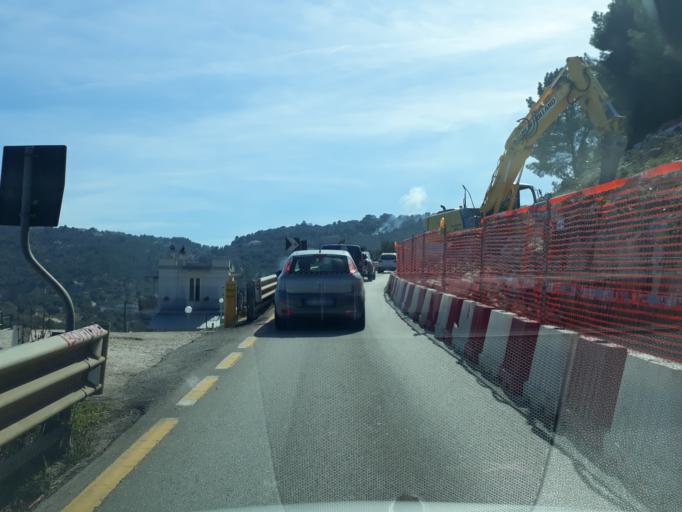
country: IT
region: Apulia
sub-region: Provincia di Brindisi
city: Lamie di Olimpie-Selva
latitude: 40.8137
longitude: 17.3465
